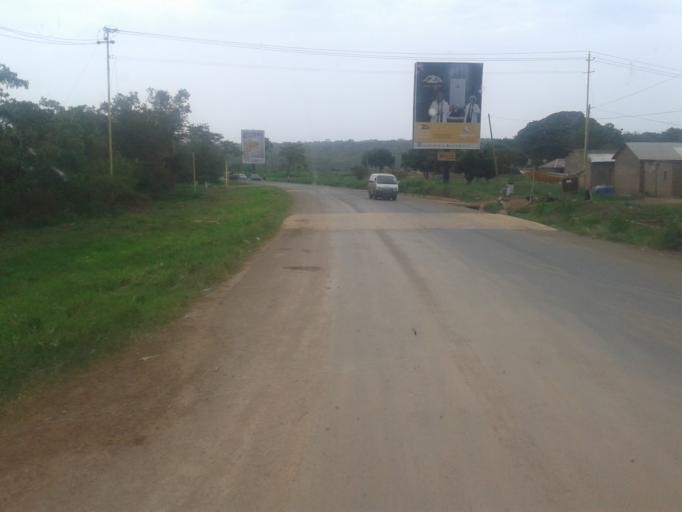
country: UG
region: Northern Region
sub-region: Oyam District
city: Oyam
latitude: 2.2357
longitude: 32.2463
